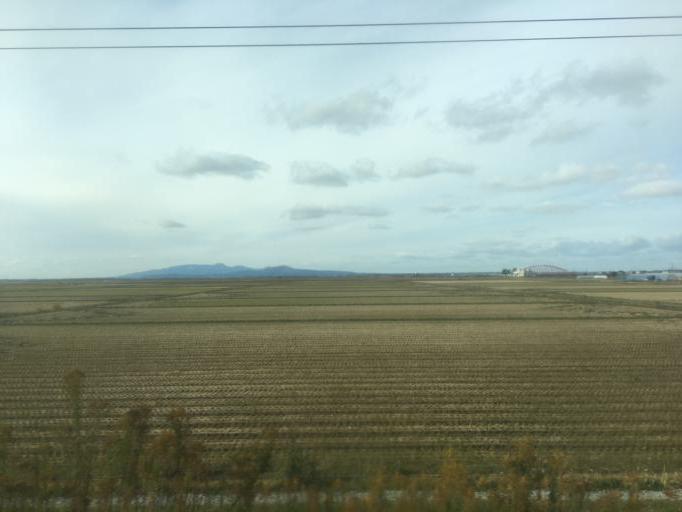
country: JP
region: Akita
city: Tenno
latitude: 39.9326
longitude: 140.0789
